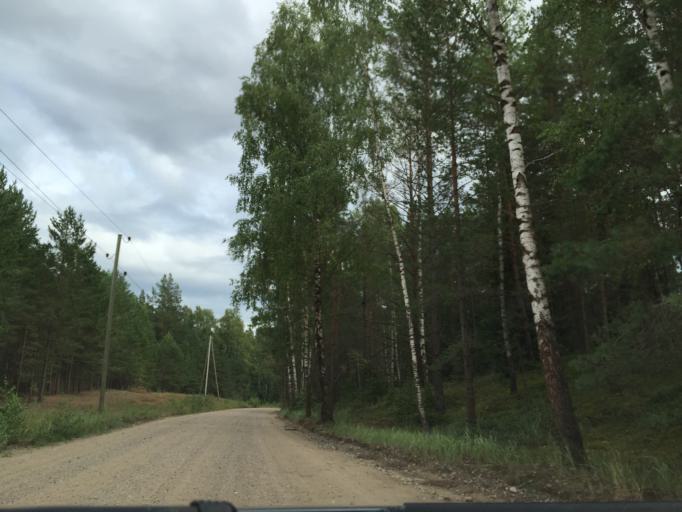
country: LV
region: Saulkrastu
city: Saulkrasti
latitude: 57.1862
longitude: 24.3683
